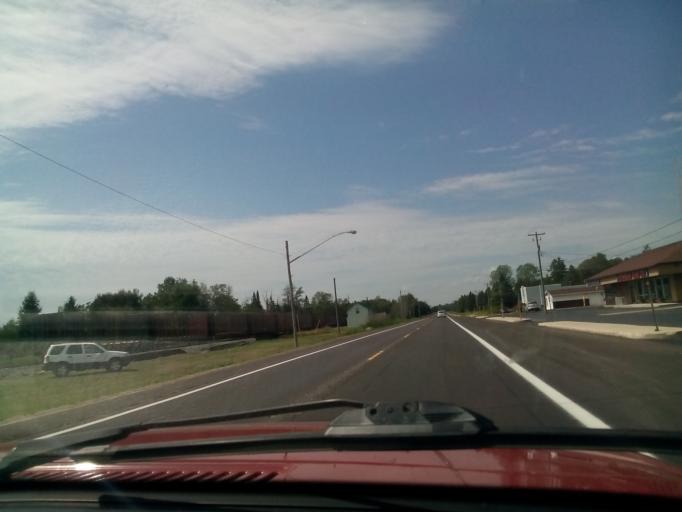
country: US
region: Michigan
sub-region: Schoolcraft County
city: Manistique
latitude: 45.9922
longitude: -86.0170
